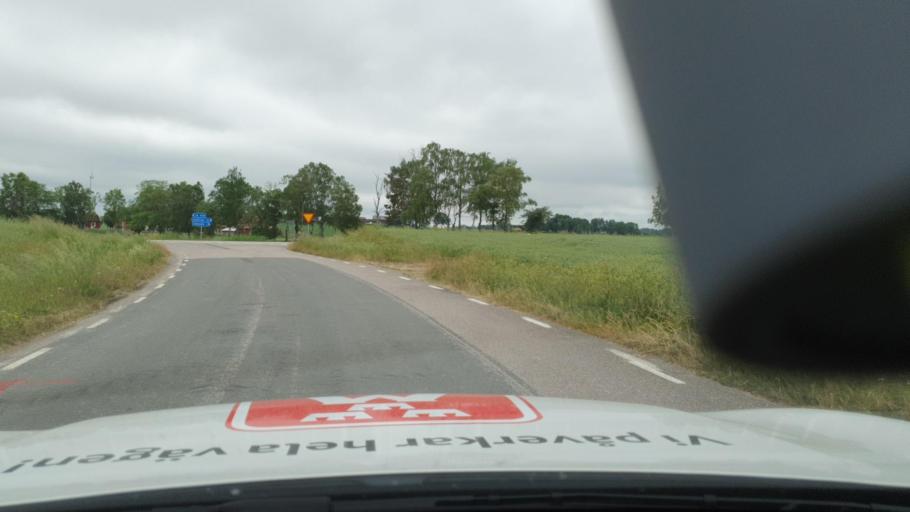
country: SE
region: Vaestra Goetaland
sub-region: Tibro Kommun
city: Tibro
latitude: 58.3527
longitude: 14.0744
